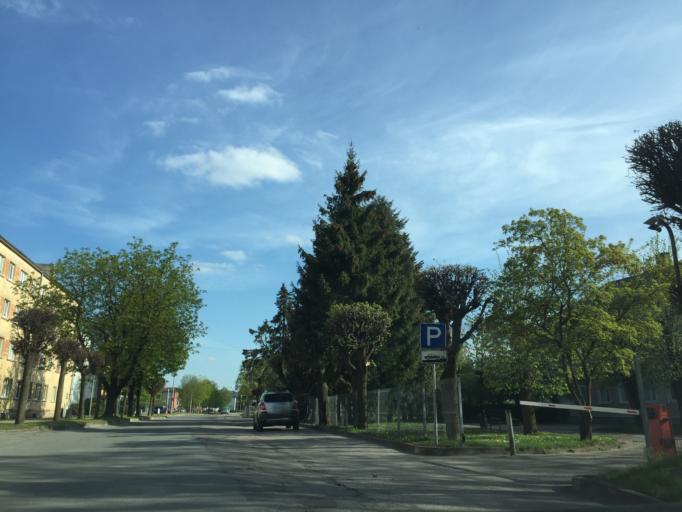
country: LV
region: Bauskas Rajons
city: Bauska
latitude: 56.4094
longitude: 24.1937
